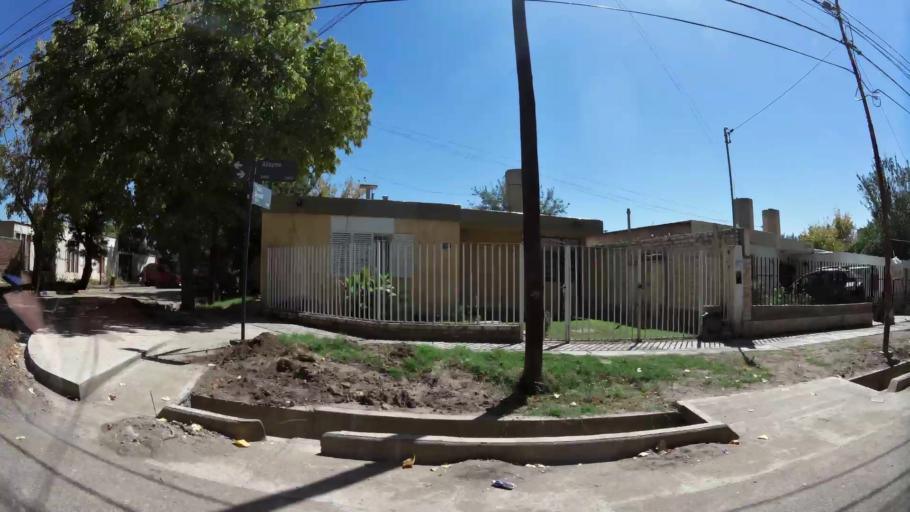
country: AR
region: Mendoza
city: Mendoza
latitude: -32.8784
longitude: -68.8062
